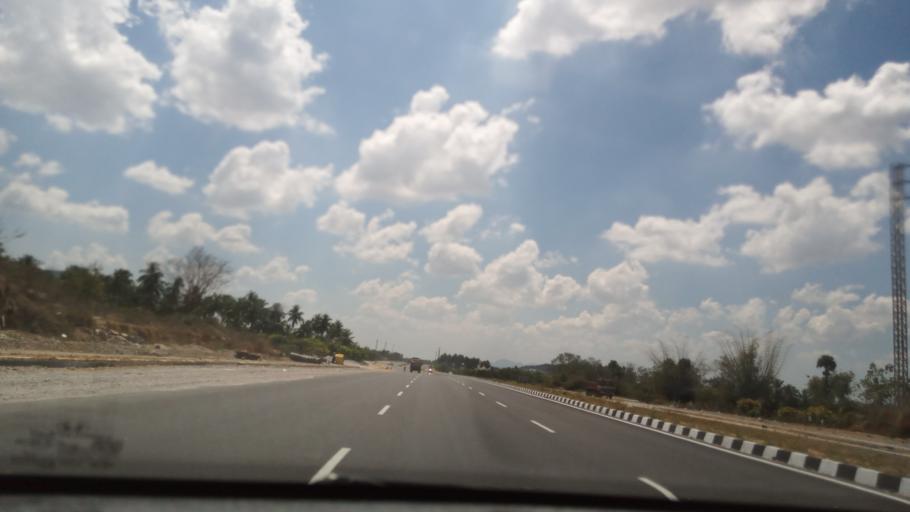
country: IN
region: Andhra Pradesh
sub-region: Chittoor
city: Pakala
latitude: 13.4489
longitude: 79.1554
